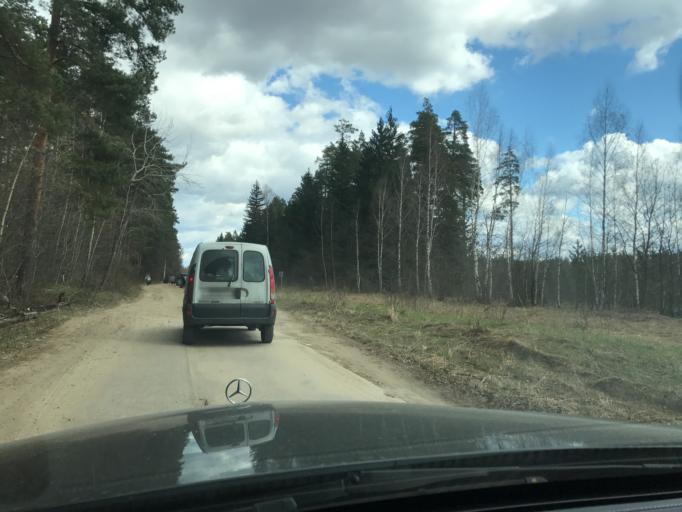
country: RU
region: Vladimir
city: Pokrov
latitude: 55.8733
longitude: 39.2411
